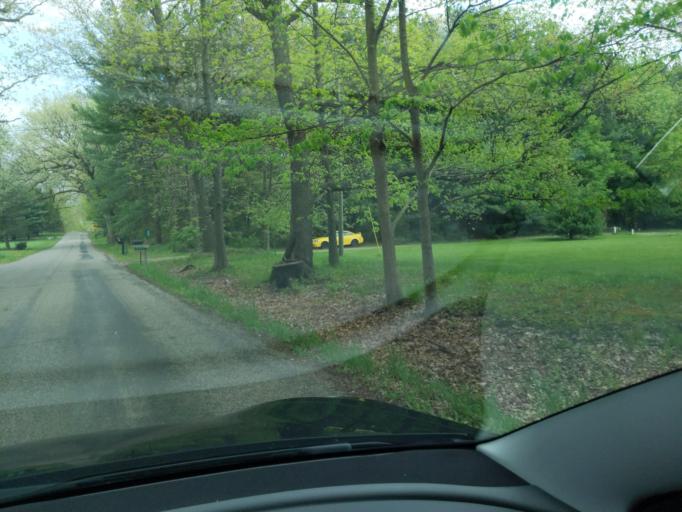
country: US
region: Michigan
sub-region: Ingham County
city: Leslie
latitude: 42.4994
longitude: -84.3339
